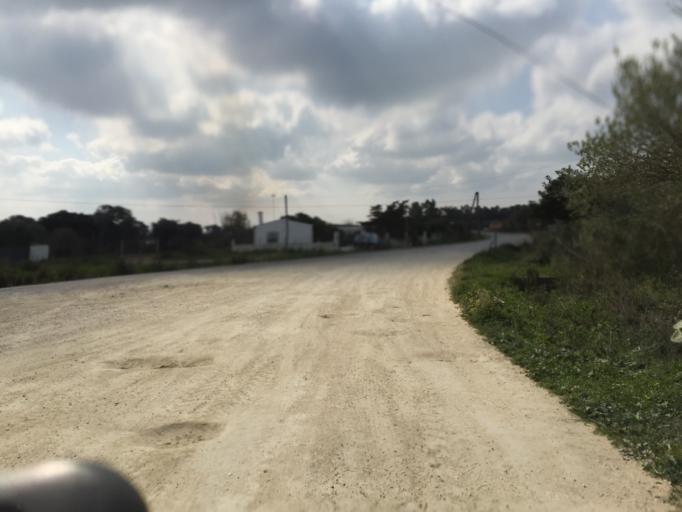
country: ES
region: Andalusia
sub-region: Provincia de Cadiz
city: Benalup-Casas Viejas
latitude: 36.3228
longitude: -5.8841
